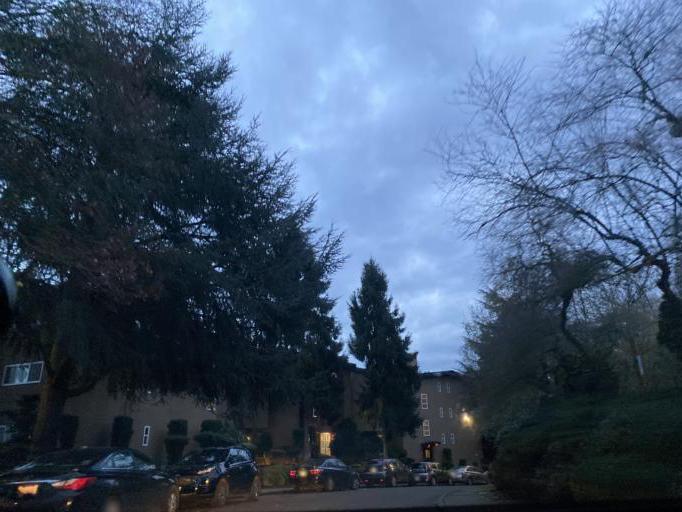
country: US
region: Washington
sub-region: King County
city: Seattle
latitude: 47.6522
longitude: -122.3899
